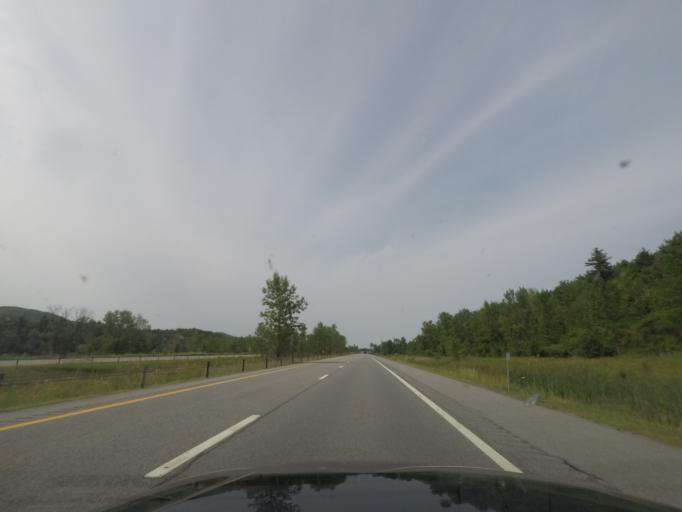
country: US
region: New York
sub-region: Essex County
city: Keeseville
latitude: 44.4315
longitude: -73.4913
